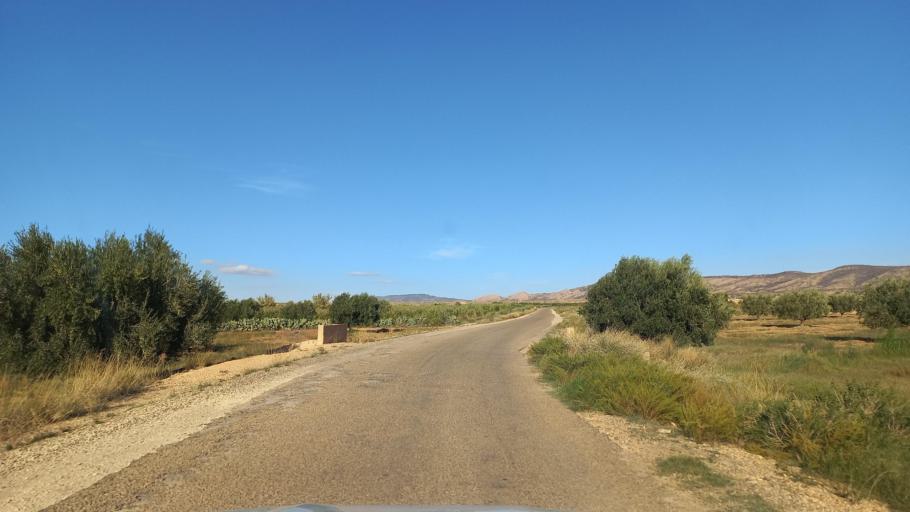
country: TN
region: Al Qasrayn
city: Sbiba
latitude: 35.3353
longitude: 9.1049
